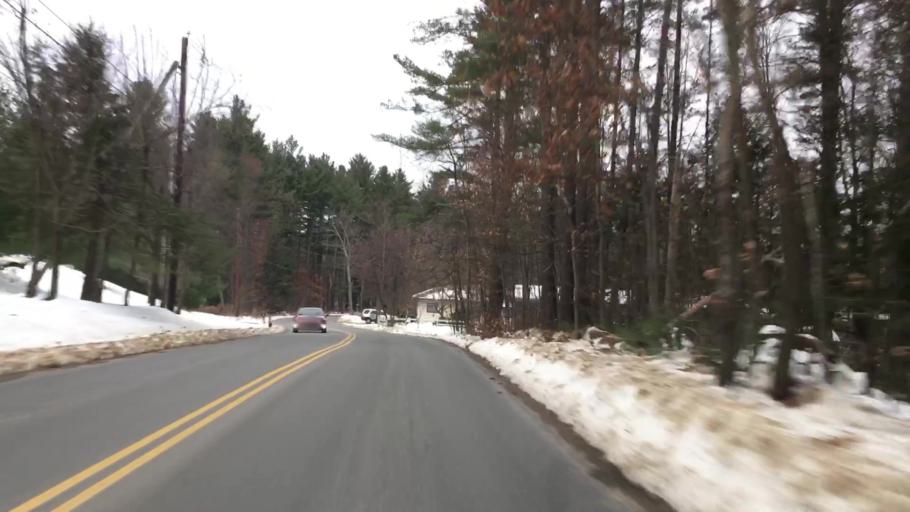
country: US
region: New Hampshire
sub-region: Hillsborough County
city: Milford
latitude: 42.8213
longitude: -71.6329
